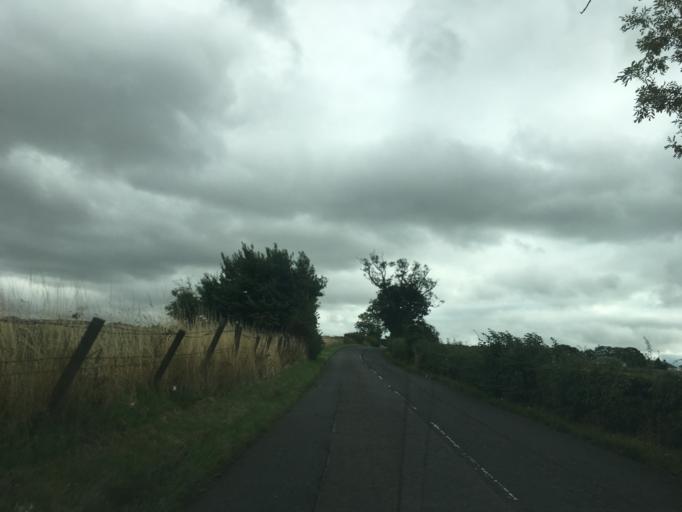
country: GB
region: Scotland
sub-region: Midlothian
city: Dalkeith
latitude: 55.8755
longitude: -3.0662
